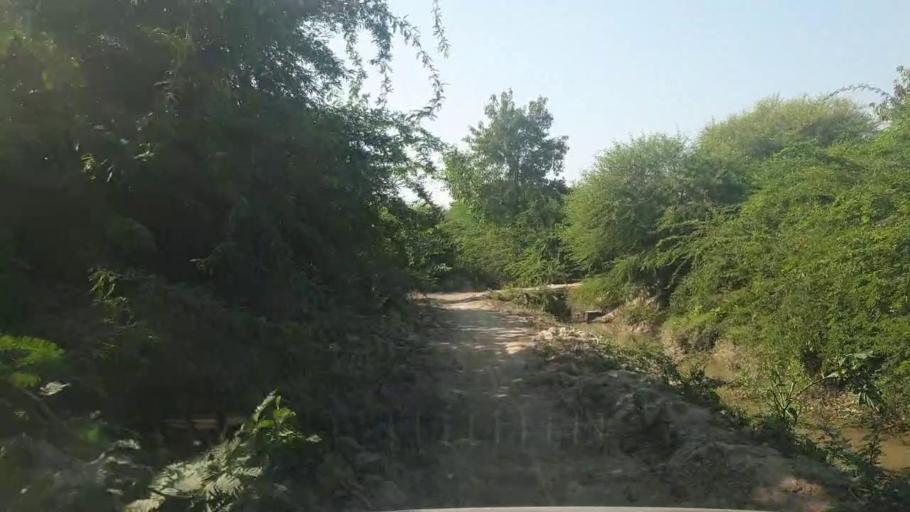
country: PK
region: Sindh
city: Badin
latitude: 24.7236
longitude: 68.8773
